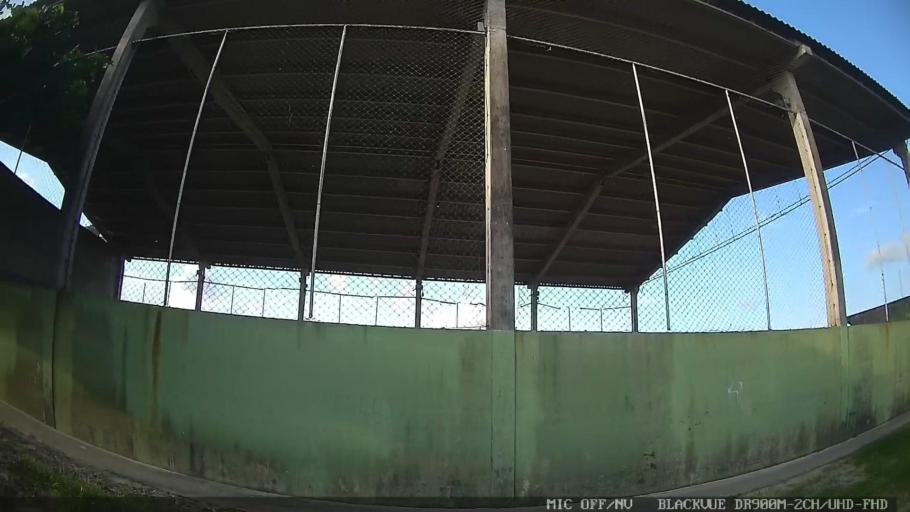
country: BR
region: Sao Paulo
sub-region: Itanhaem
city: Itanhaem
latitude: -24.1827
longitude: -46.8311
